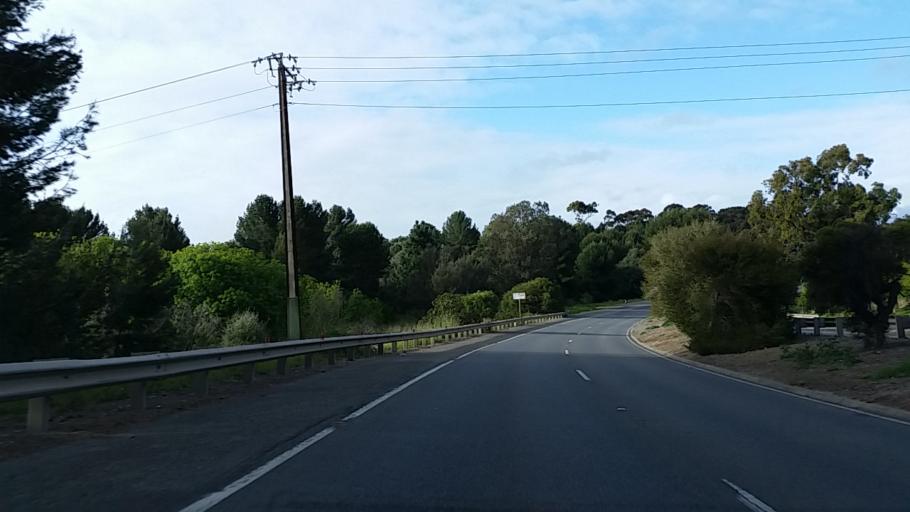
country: AU
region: South Australia
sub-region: Marion
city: Happy Valley
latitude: -35.0897
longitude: 138.5376
